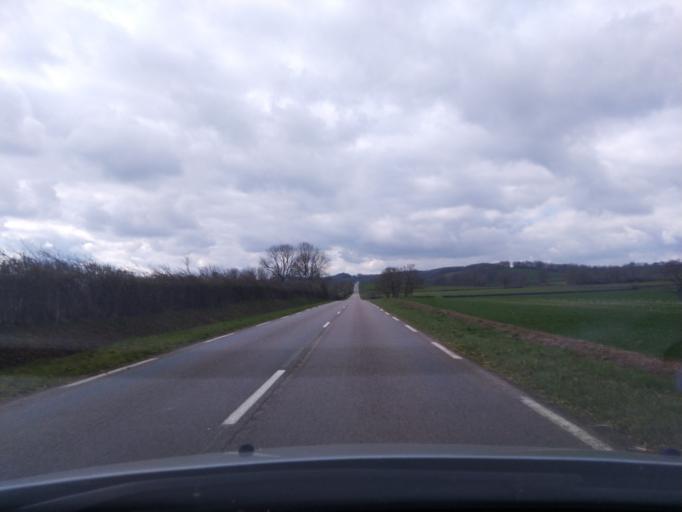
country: FR
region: Bourgogne
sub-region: Departement de l'Yonne
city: Avallon
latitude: 47.5385
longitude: 4.0269
